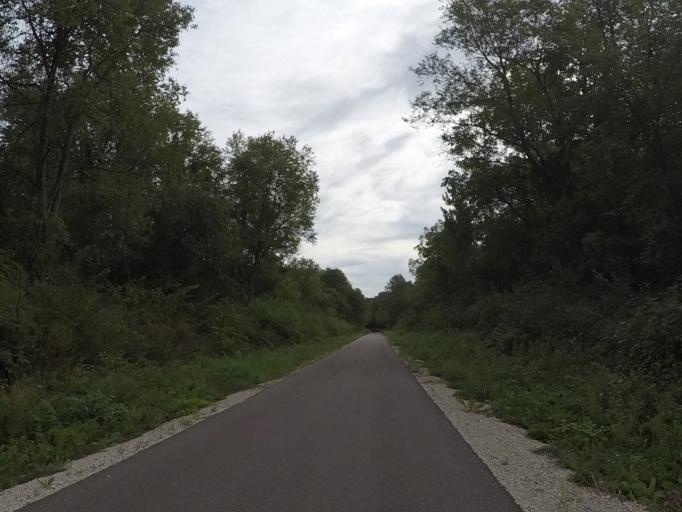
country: US
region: Wisconsin
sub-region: Sauk County
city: Baraboo
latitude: 43.3821
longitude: -89.7217
